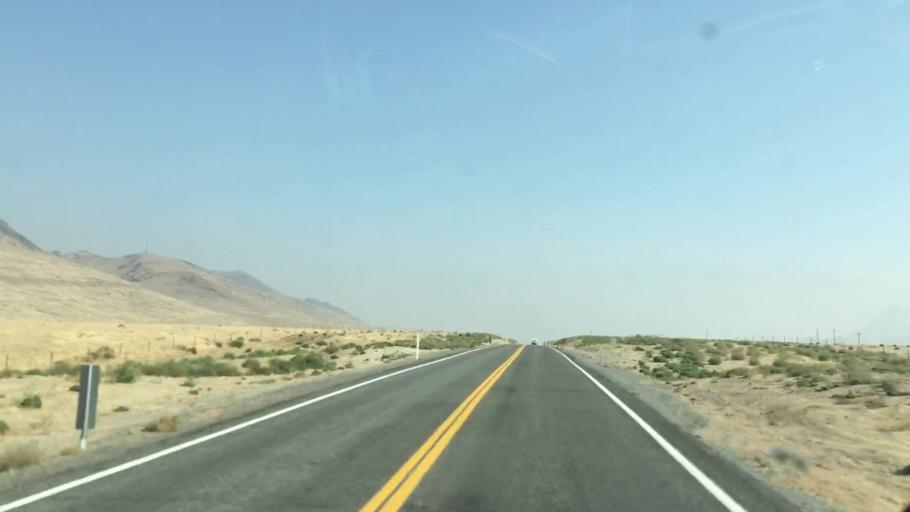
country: US
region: Nevada
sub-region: Lyon County
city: Fernley
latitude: 40.3849
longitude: -119.3330
